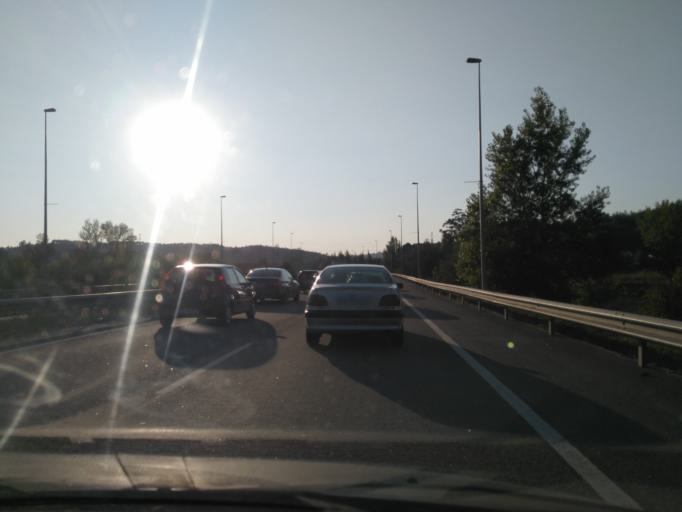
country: PT
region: Braga
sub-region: Guimaraes
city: Candoso
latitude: 41.4381
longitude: -8.3207
